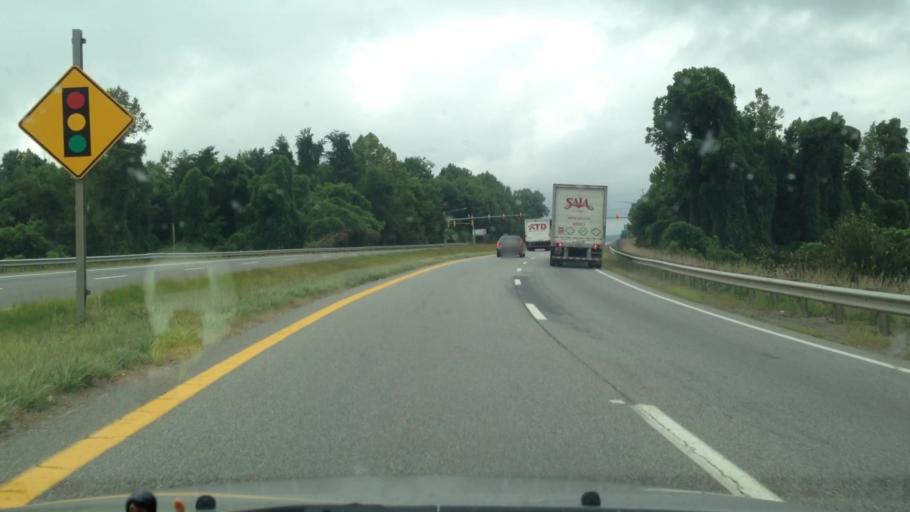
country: US
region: Virginia
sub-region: Henry County
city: Chatmoss
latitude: 36.5851
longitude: -79.8633
